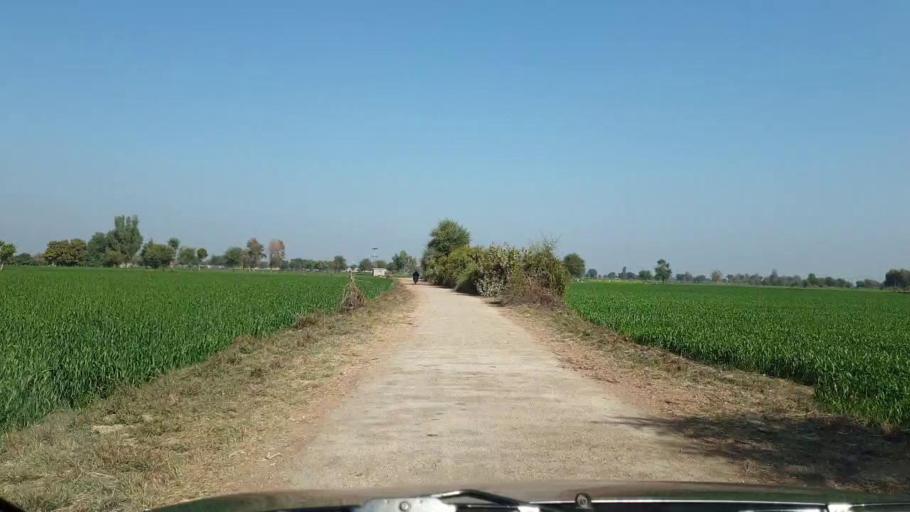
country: PK
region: Sindh
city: Sinjhoro
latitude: 25.9397
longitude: 68.7634
